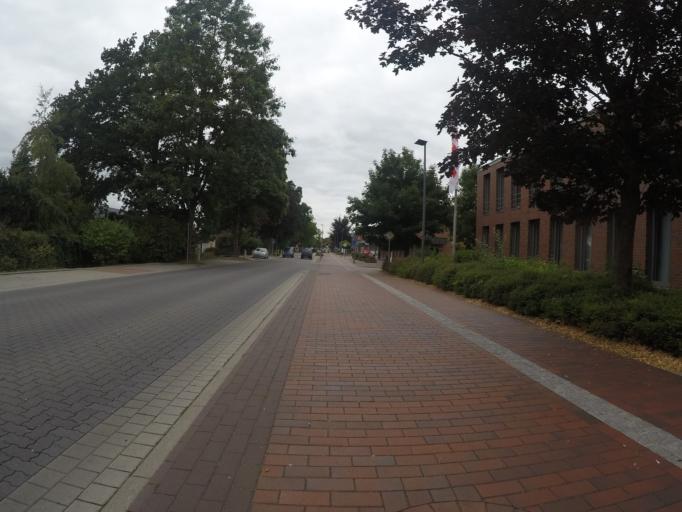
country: DE
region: Lower Saxony
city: Hemmoor
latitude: 53.6868
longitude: 9.1567
